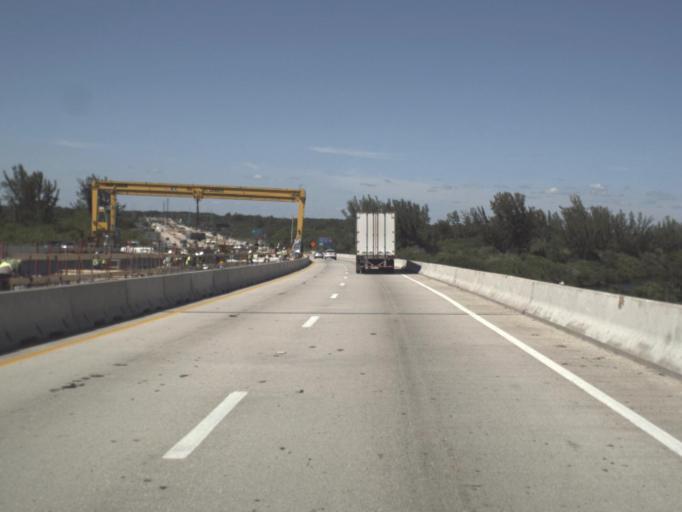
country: US
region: Florida
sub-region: Lee County
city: Tice
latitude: 26.6995
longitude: -81.7999
